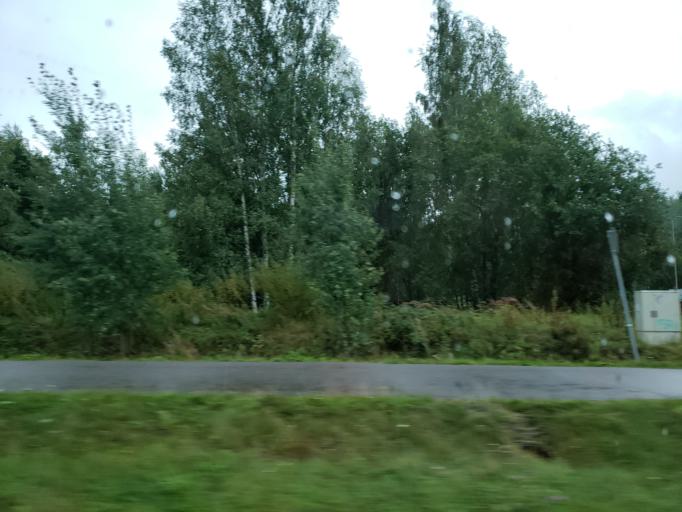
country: FI
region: Uusimaa
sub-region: Porvoo
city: Porvoo
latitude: 60.3854
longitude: 25.6489
